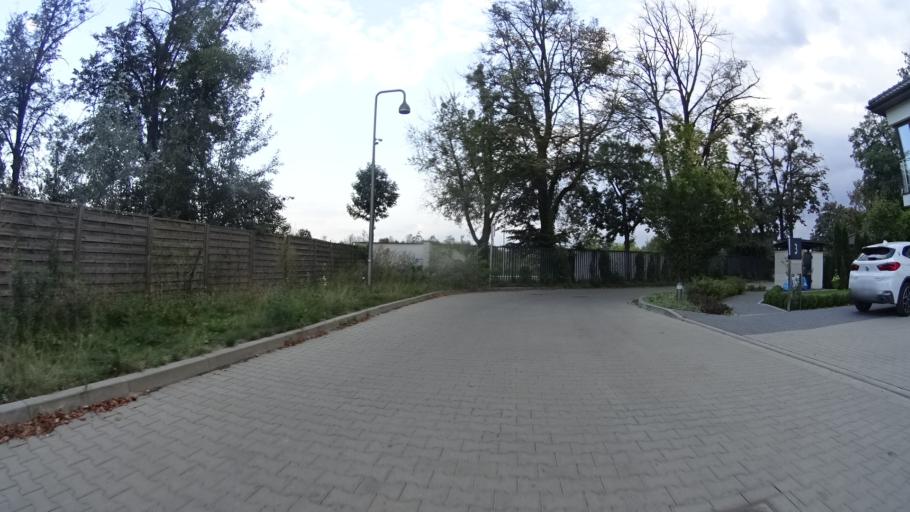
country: PL
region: Masovian Voivodeship
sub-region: Powiat warszawski zachodni
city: Ozarow Mazowiecki
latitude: 52.2315
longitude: 20.8055
